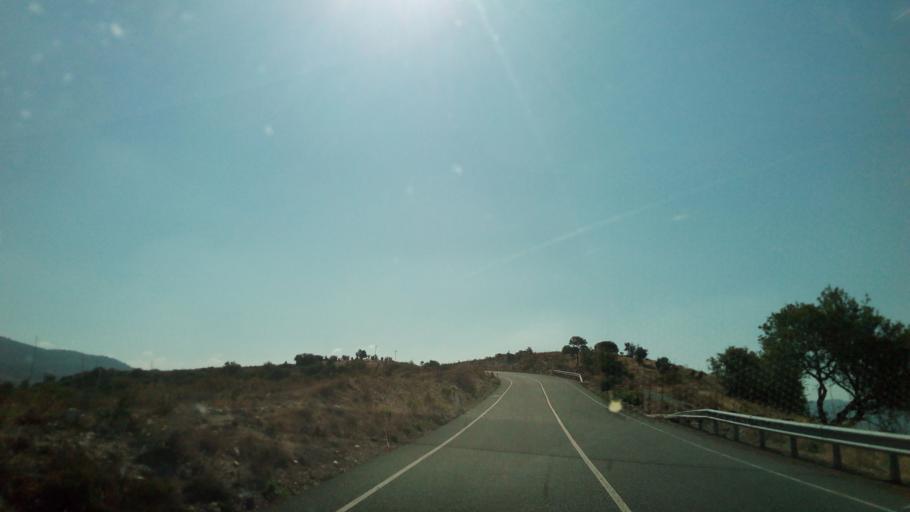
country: CY
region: Limassol
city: Pissouri
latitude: 34.7903
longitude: 32.6292
